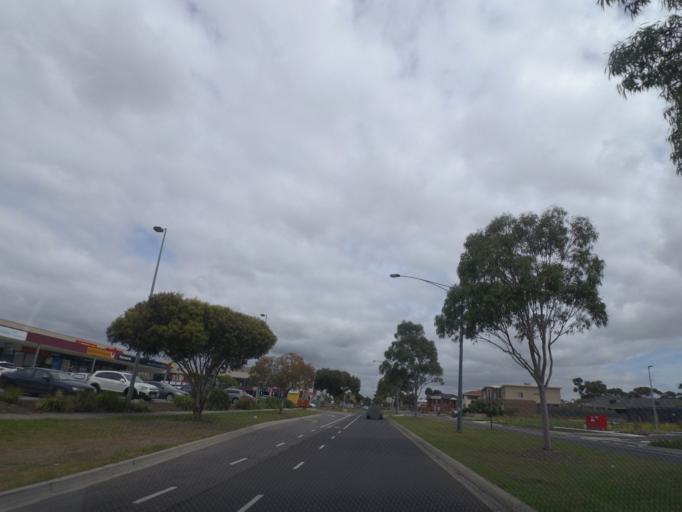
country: AU
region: Victoria
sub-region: Brimbank
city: Cairnlea
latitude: -37.7578
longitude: 144.7903
